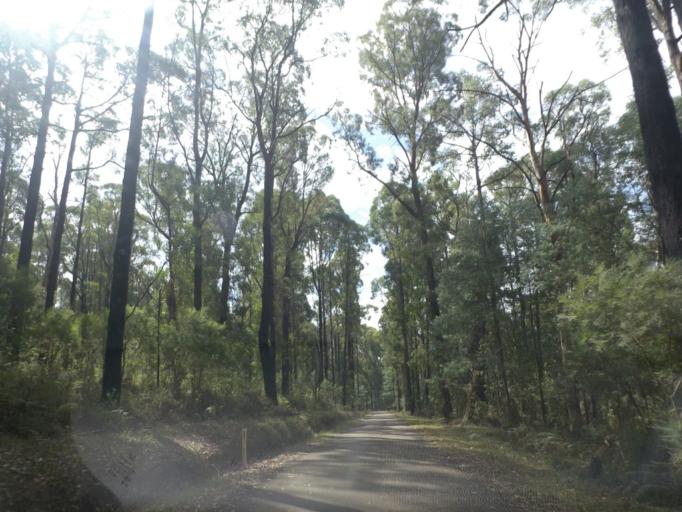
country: AU
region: Victoria
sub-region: Yarra Ranges
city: Millgrove
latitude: -37.5719
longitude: 145.6880
